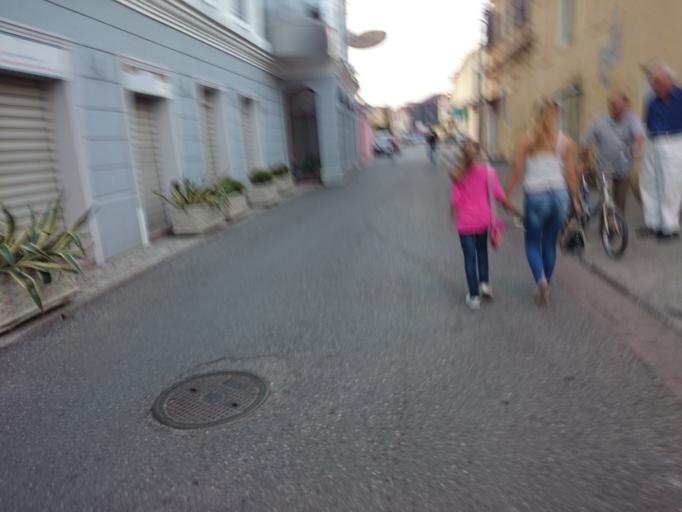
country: AL
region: Shkoder
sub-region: Rrethi i Shkodres
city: Shkoder
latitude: 42.0642
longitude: 19.5197
